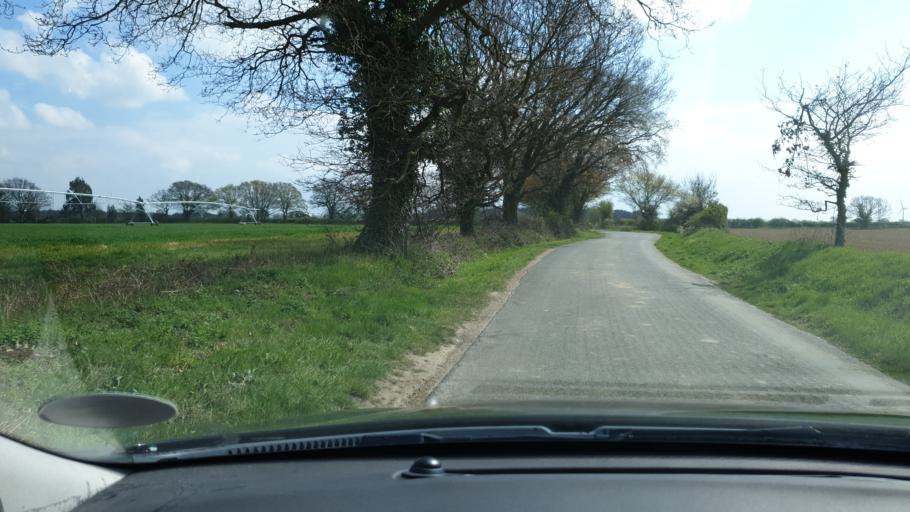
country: GB
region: England
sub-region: Essex
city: Great Bentley
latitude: 51.8400
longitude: 1.0823
